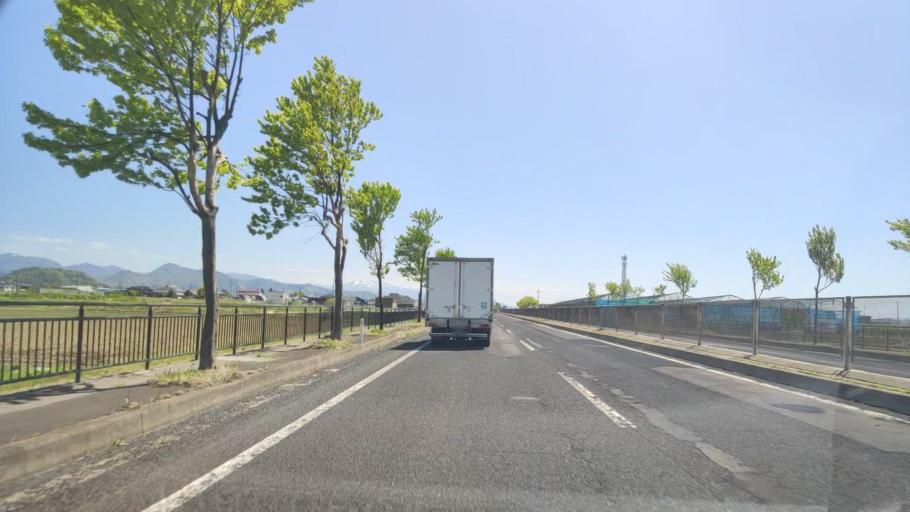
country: JP
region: Yamagata
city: Higashine
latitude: 38.4557
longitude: 140.3824
